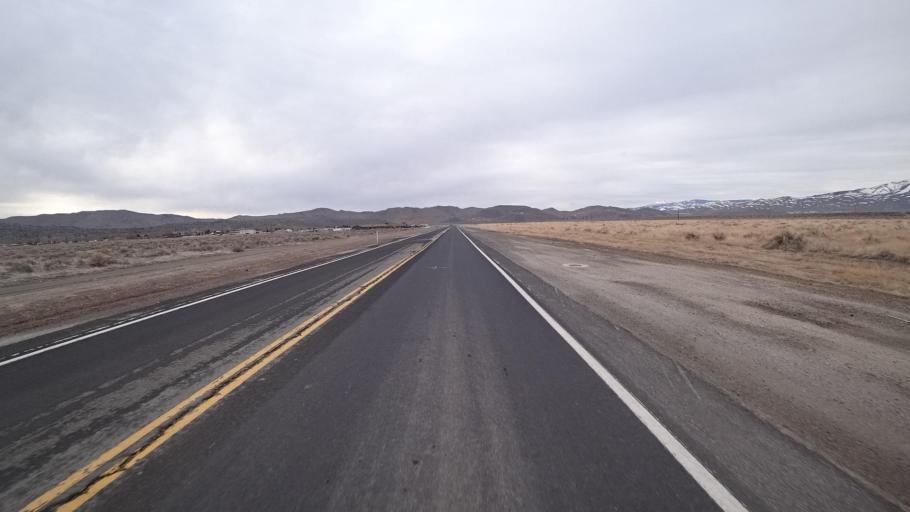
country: US
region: Nevada
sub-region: Washoe County
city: Lemmon Valley
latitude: 39.6676
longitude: -119.8312
